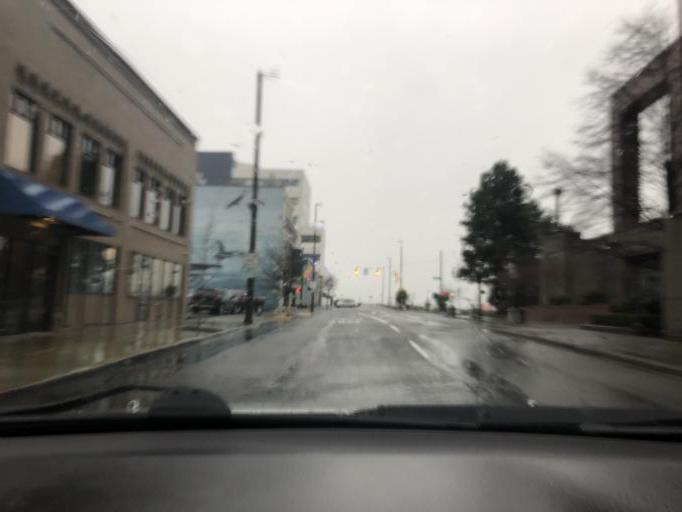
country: US
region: Washington
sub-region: Pierce County
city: Tacoma
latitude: 47.2549
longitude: -122.4375
